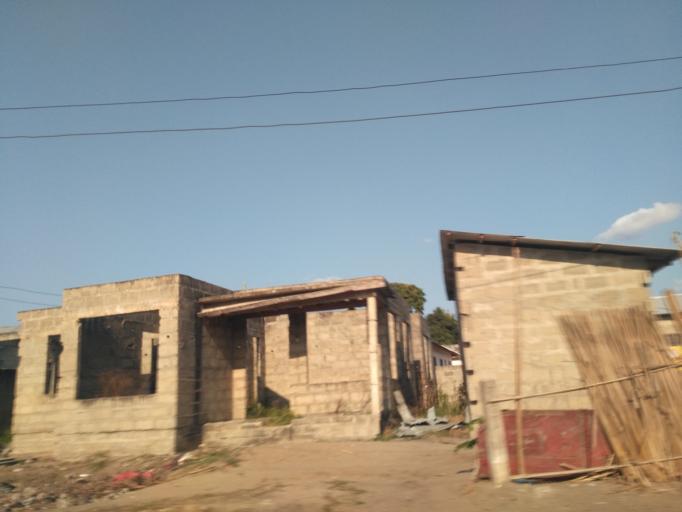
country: TZ
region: Dar es Salaam
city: Dar es Salaam
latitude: -6.8519
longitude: 39.3172
